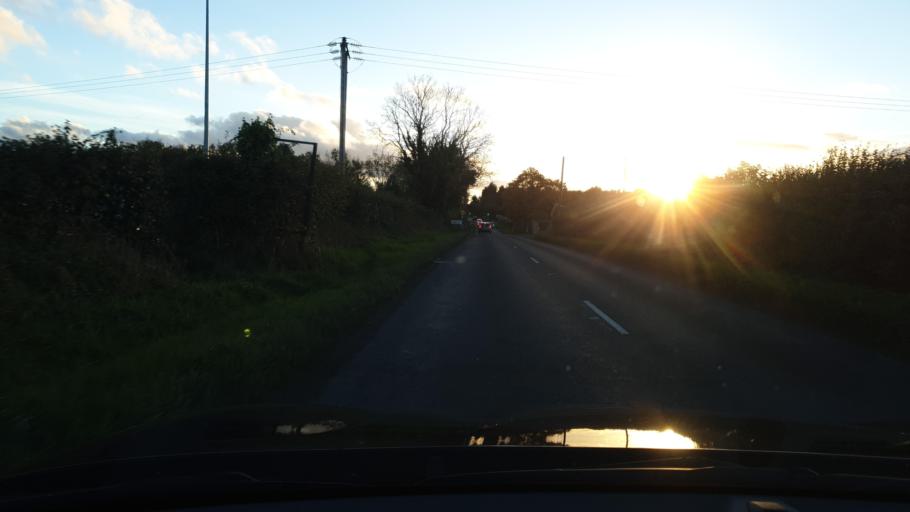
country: IE
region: Leinster
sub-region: Lu
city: Drogheda
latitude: 53.7296
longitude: -6.3221
